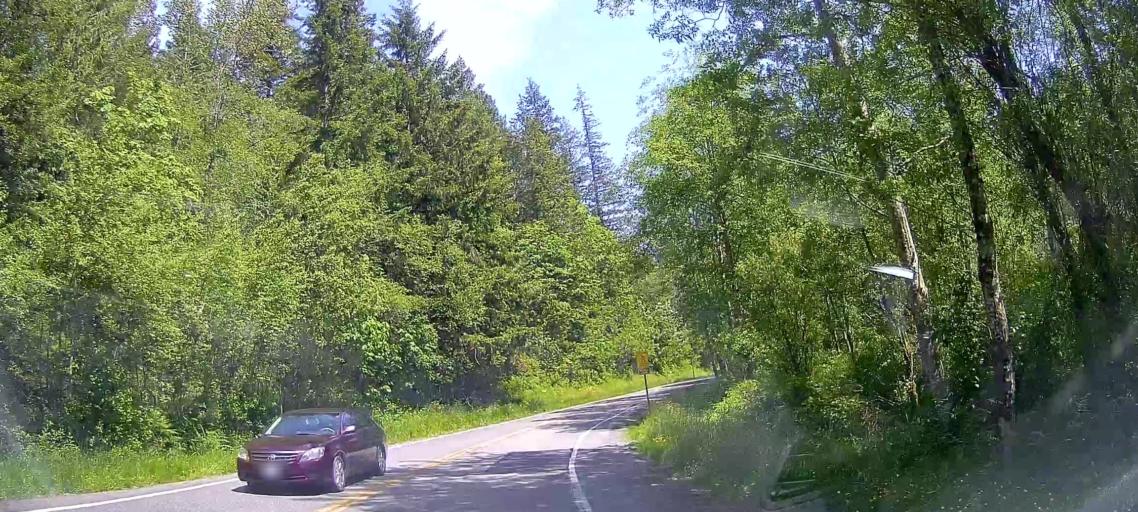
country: US
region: Washington
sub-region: Skagit County
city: Mount Vernon
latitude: 48.3982
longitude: -122.2965
